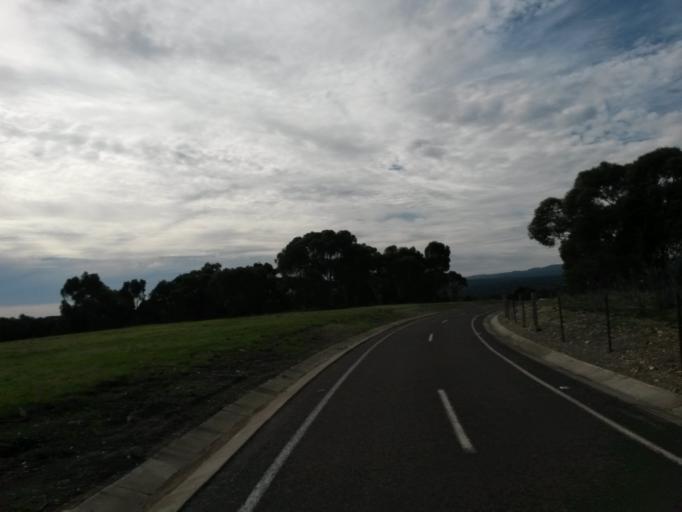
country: AU
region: South Australia
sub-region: Onkaparinga
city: Bedford Park
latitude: -35.0470
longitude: 138.5509
